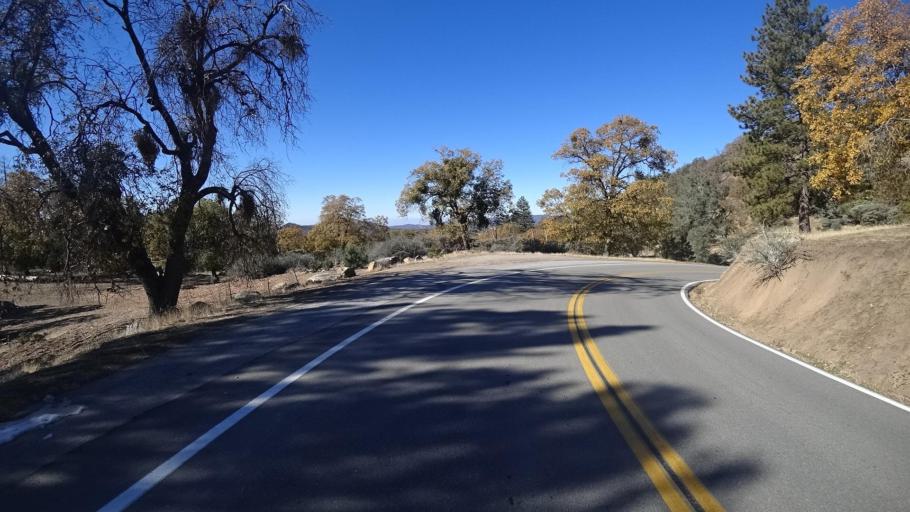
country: US
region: California
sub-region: Kern County
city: Alta Sierra
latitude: 35.7371
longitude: -118.6125
